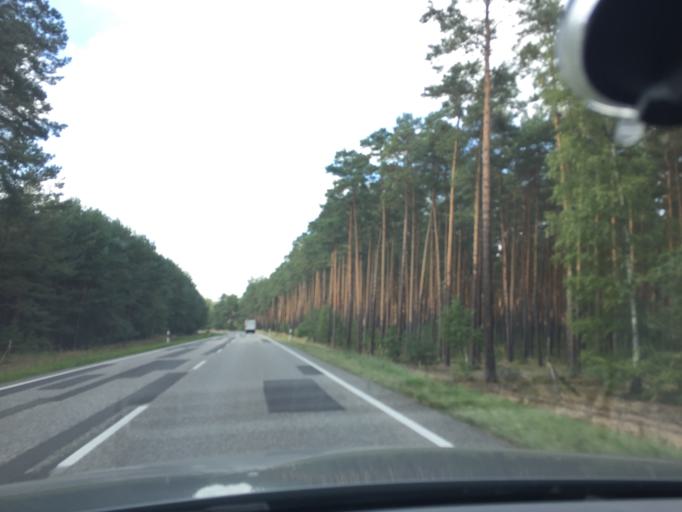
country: DE
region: Brandenburg
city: Grunheide
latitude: 52.3926
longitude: 13.8187
